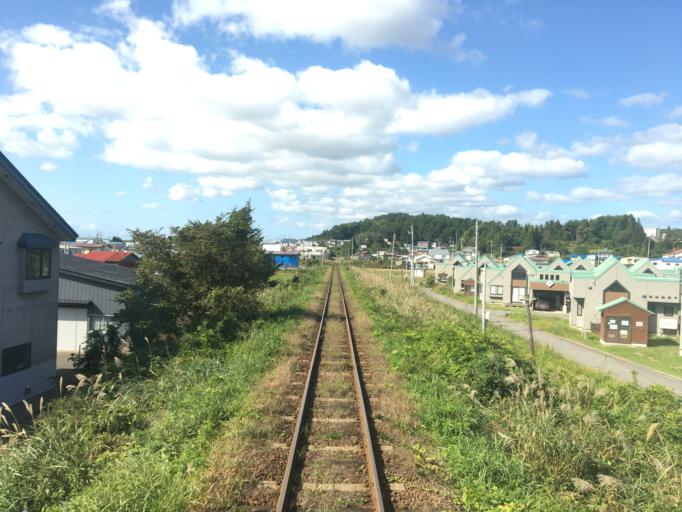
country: JP
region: Aomori
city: Goshogawara
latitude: 40.9616
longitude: 140.4427
